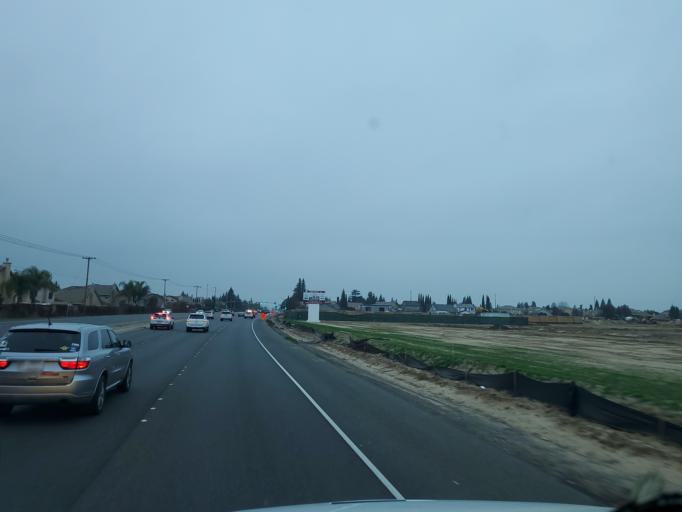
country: US
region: California
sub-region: Stanislaus County
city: Del Rio
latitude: 37.7005
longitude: -121.0186
